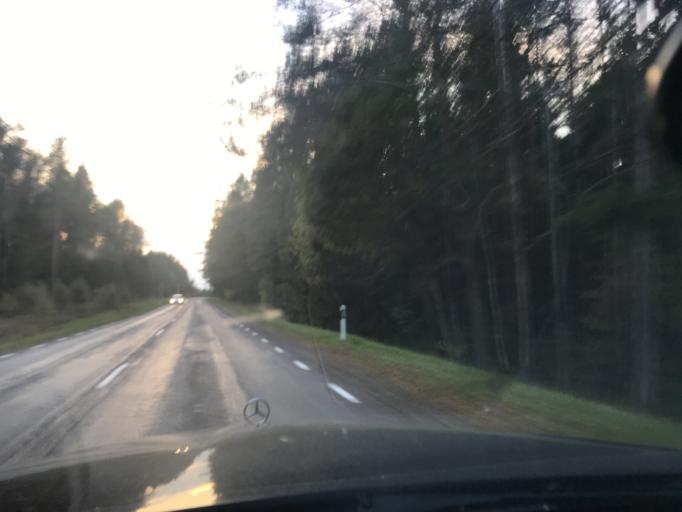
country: EE
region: Valgamaa
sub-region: Torva linn
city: Torva
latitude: 58.0095
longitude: 26.1566
